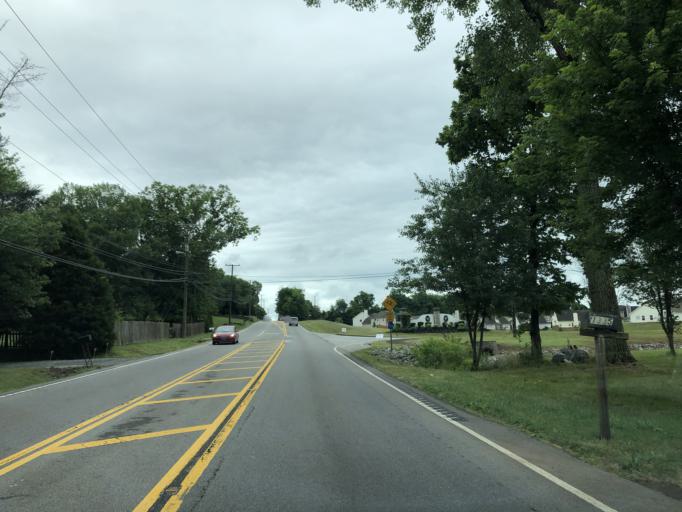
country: US
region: Tennessee
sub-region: Davidson County
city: Goodlettsville
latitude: 36.2777
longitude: -86.7704
